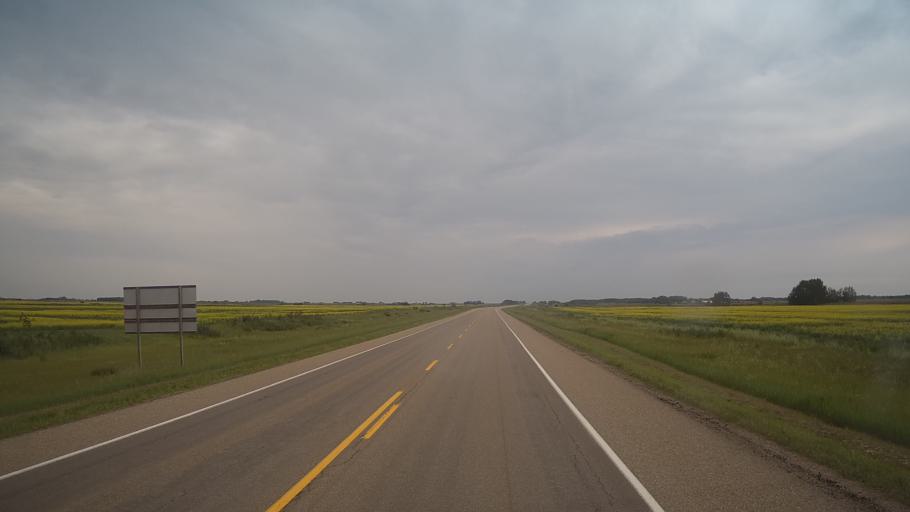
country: CA
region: Saskatchewan
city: Langham
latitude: 52.1281
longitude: -107.2439
